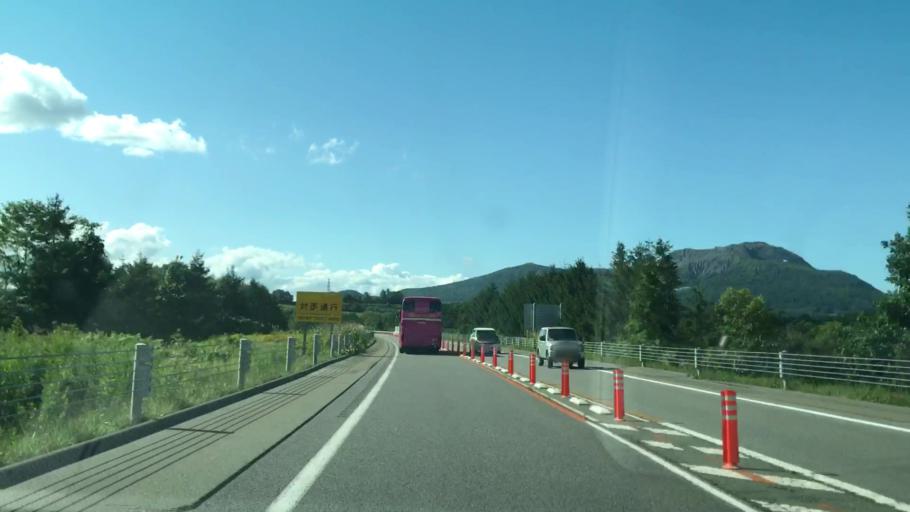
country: JP
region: Hokkaido
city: Date
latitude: 42.4930
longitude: 140.8762
